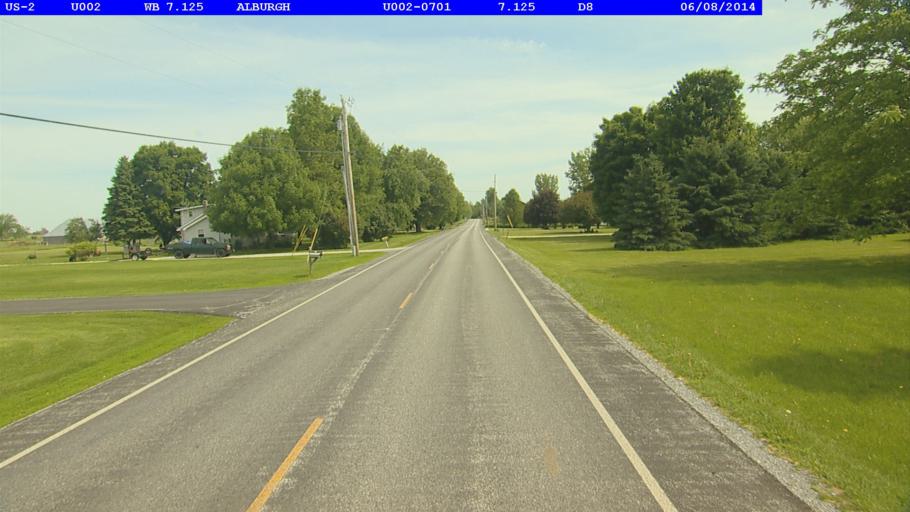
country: US
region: New York
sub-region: Clinton County
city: Rouses Point
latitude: 44.9483
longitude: -73.2728
